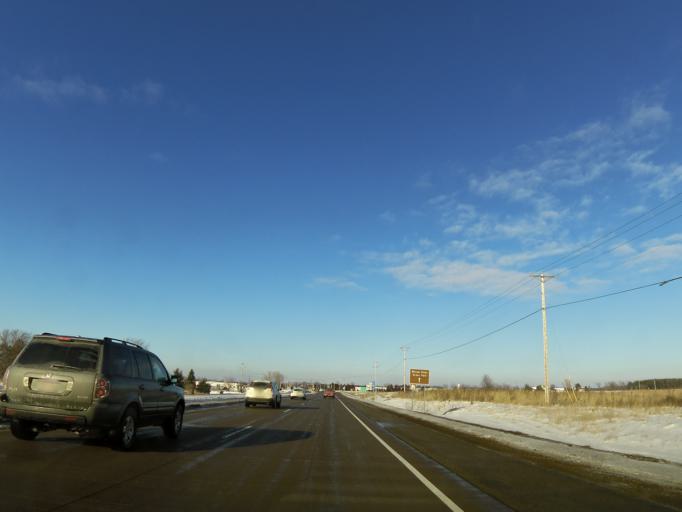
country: US
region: Wisconsin
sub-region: Saint Croix County
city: North Hudson
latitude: 44.9839
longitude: -92.6800
